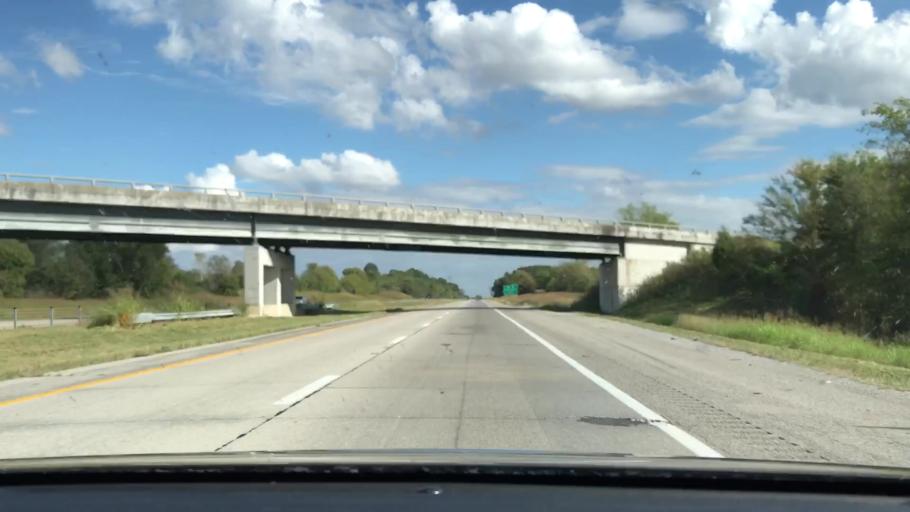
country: US
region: Kentucky
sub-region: Trigg County
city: Cadiz
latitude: 36.8946
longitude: -87.7561
